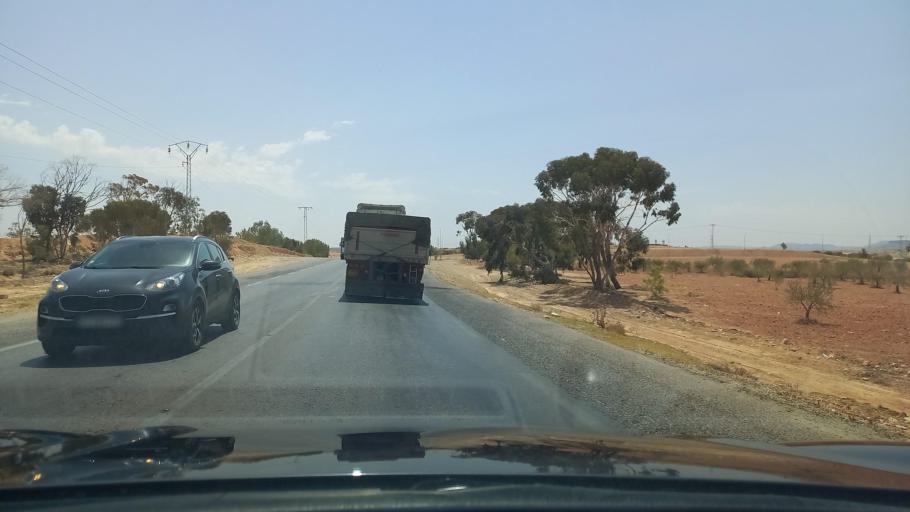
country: TN
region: Madanin
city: Medenine
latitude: 33.5682
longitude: 10.3171
